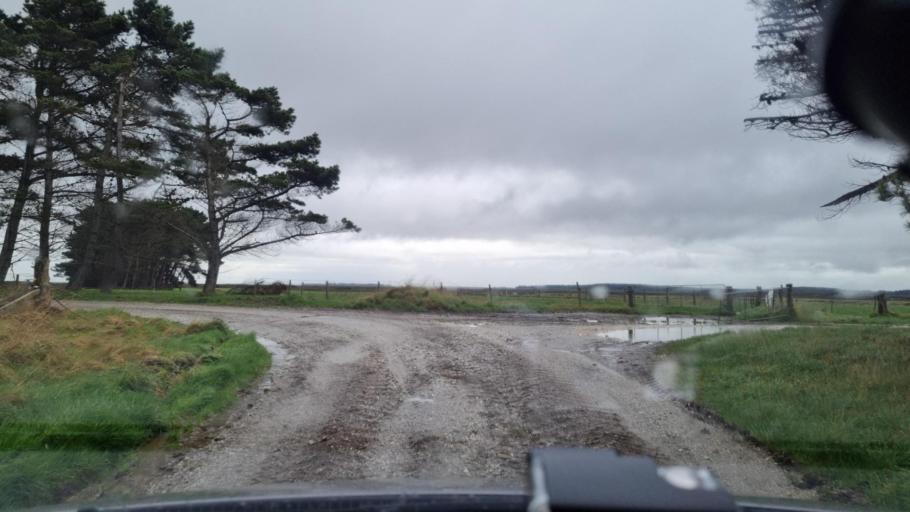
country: NZ
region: Southland
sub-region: Invercargill City
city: Bluff
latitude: -46.5671
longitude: 168.5020
